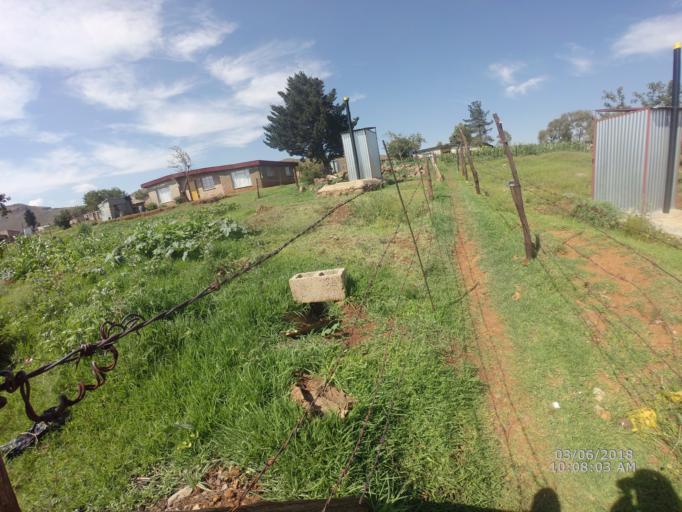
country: LS
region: Berea
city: Teyateyaneng
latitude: -29.2268
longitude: 27.8657
